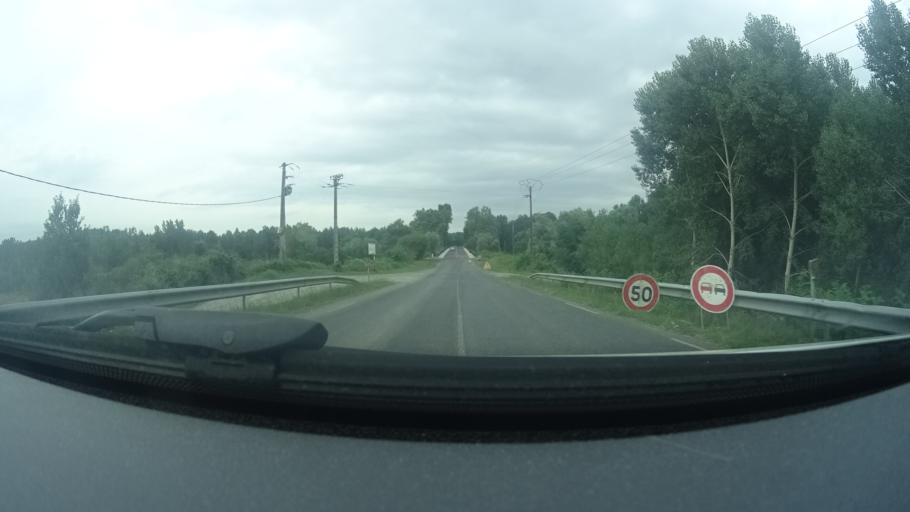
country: FR
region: Aquitaine
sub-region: Departement des Pyrenees-Atlantiques
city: Mont
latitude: 43.4496
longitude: -0.6865
